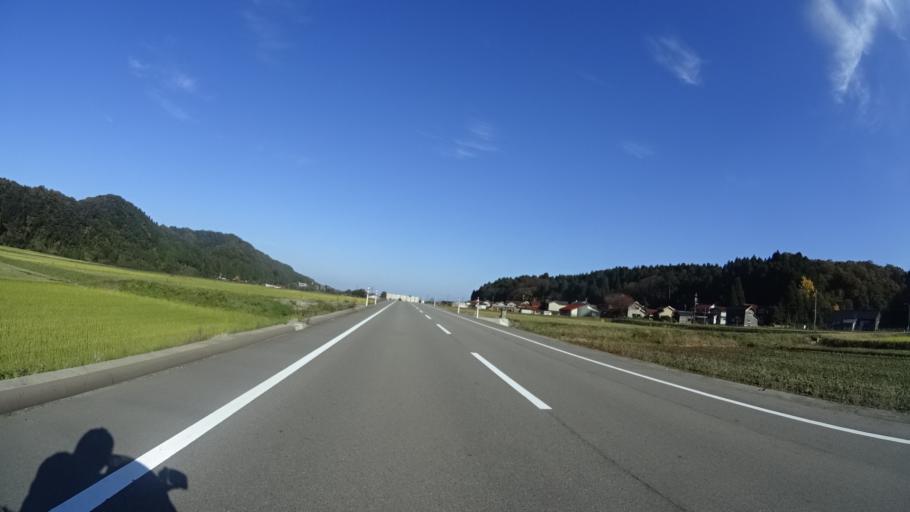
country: JP
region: Ishikawa
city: Komatsu
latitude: 36.2676
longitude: 136.3936
